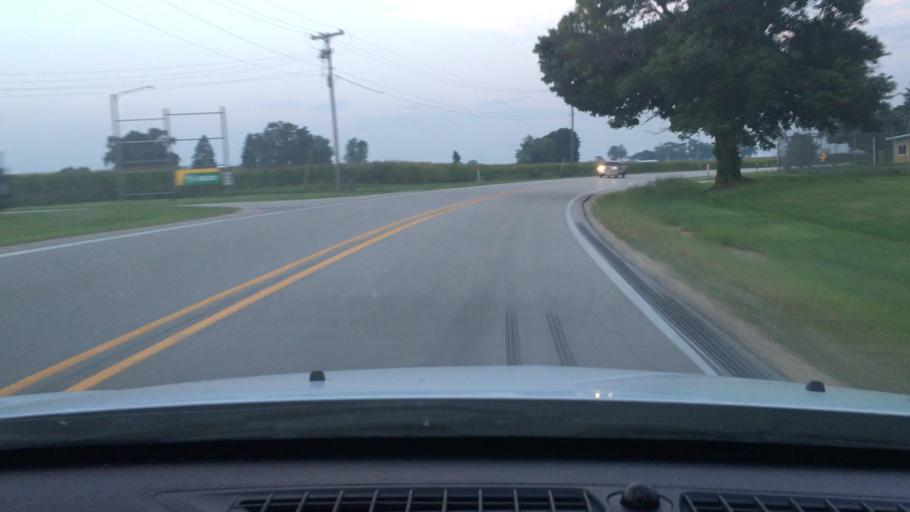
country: US
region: Illinois
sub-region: Ogle County
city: Rochelle
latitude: 41.8936
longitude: -89.0685
